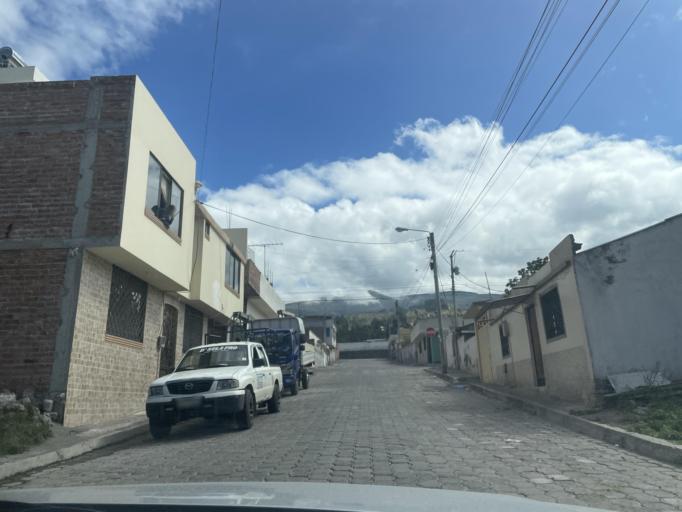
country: EC
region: Chimborazo
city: Guano
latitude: -1.6037
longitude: -78.6436
